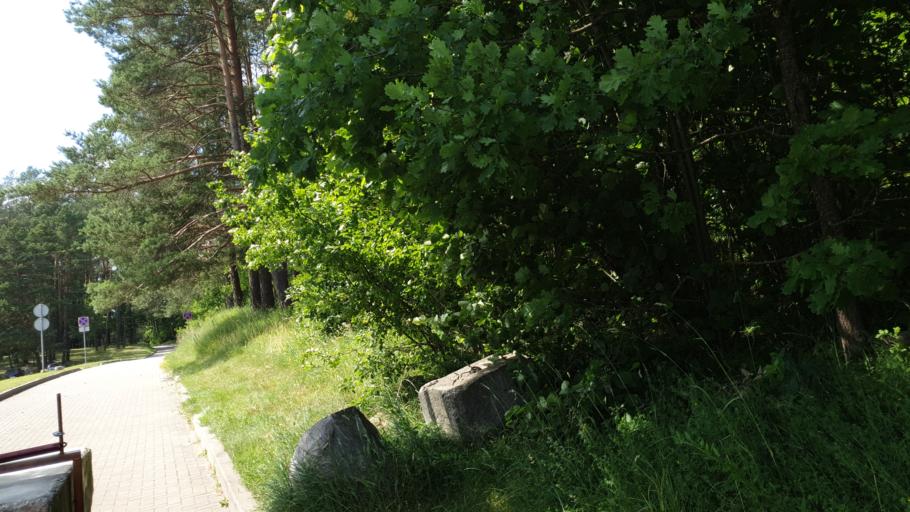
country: LT
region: Vilnius County
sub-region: Vilnius
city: Fabijoniskes
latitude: 54.7929
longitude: 25.3031
